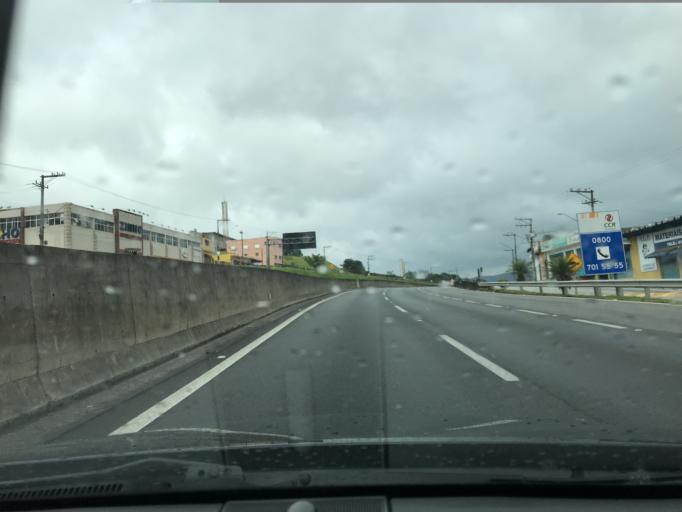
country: BR
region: Sao Paulo
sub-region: Vargem Grande Paulista
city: Vargem Grande Paulista
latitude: -23.6119
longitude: -47.0049
